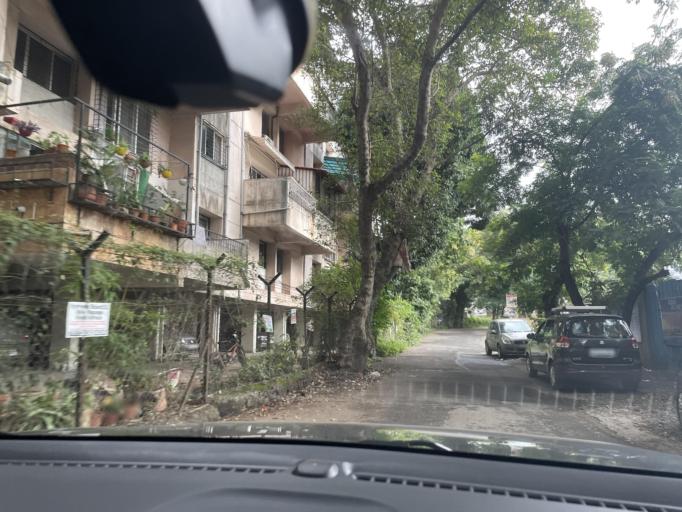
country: IN
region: Maharashtra
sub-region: Pune Division
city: Kharakvasla
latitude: 18.5125
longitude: 73.7804
